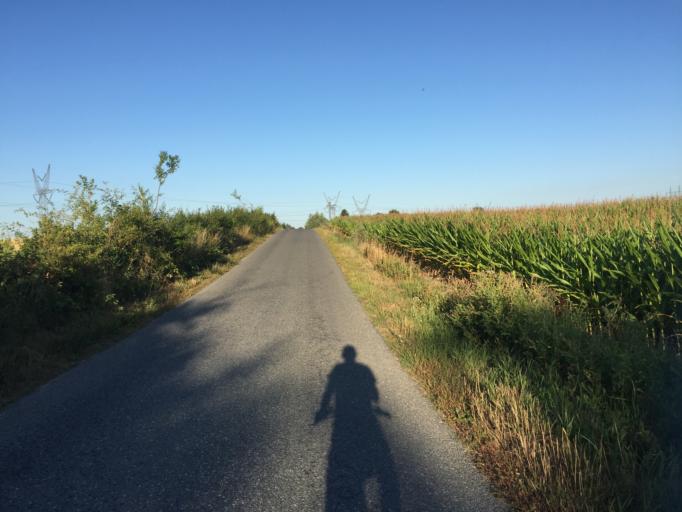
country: DK
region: South Denmark
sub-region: Odense Kommune
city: Bellinge
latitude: 55.3685
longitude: 10.2860
